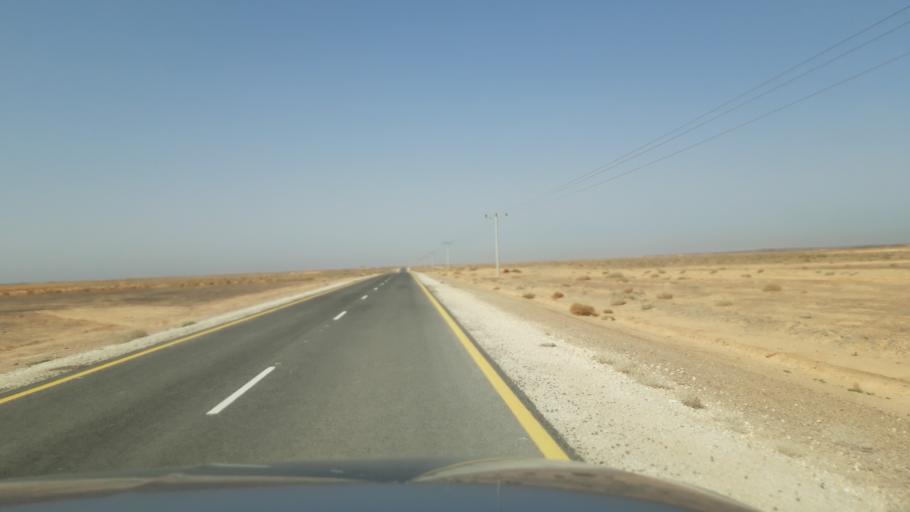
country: JO
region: Amman
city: Al Azraq ash Shamali
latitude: 31.7787
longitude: 36.7813
